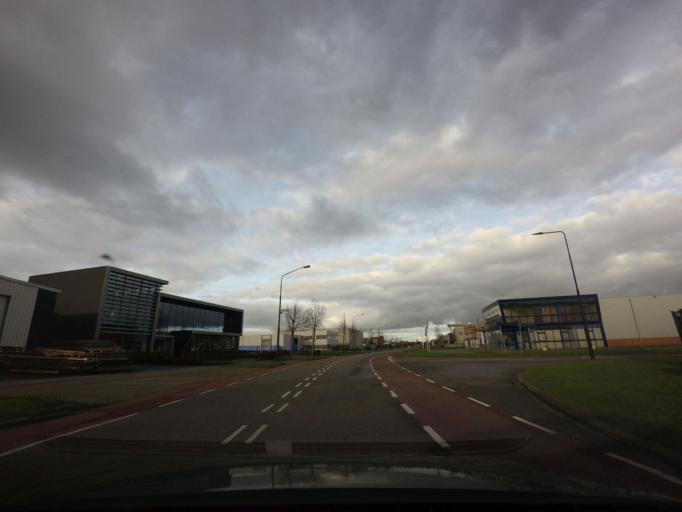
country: NL
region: North Holland
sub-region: Gemeente Heerhugowaard
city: Heerhugowaard
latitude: 52.6876
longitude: 4.8341
